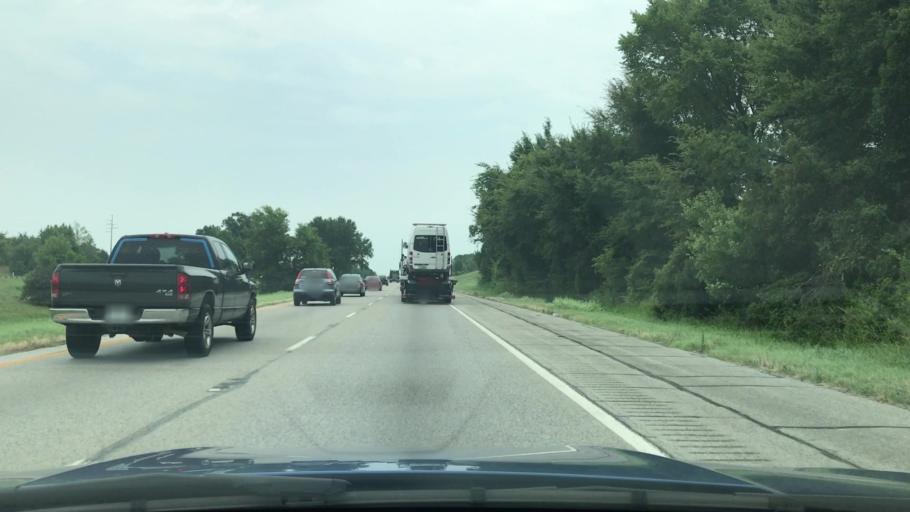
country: US
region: Texas
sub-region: Smith County
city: Hideaway
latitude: 32.4801
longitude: -95.4962
